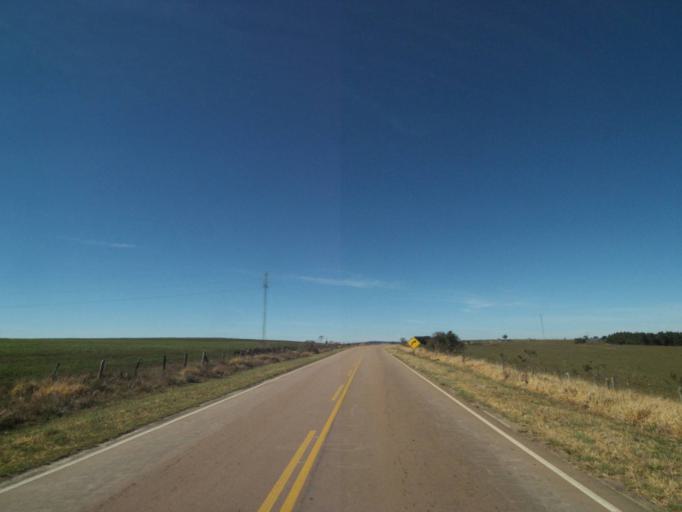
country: BR
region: Parana
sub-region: Tibagi
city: Tibagi
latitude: -24.6345
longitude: -50.2341
